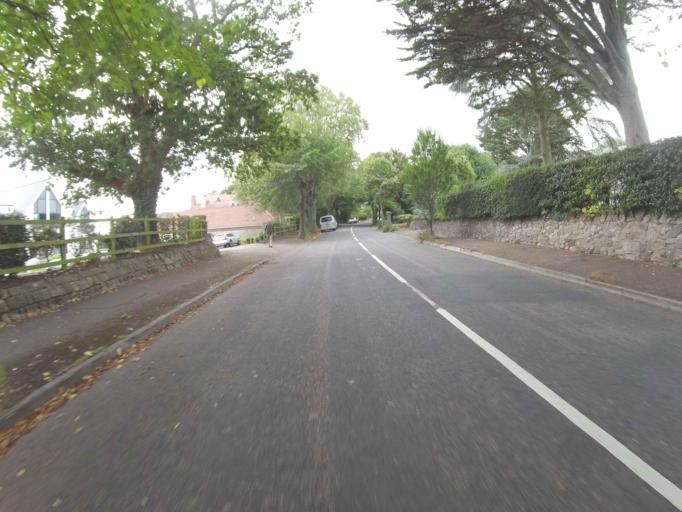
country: GB
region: England
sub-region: Devon
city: Exmouth
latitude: 50.6166
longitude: -3.3934
